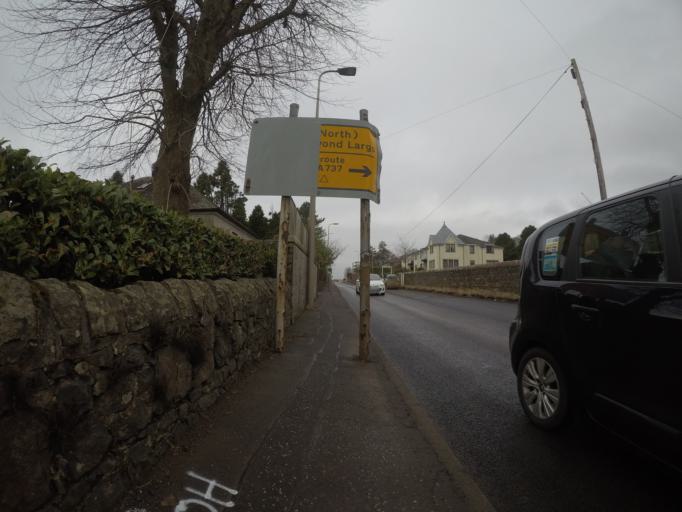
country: GB
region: Scotland
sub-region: North Ayrshire
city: Largs
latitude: 55.7834
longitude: -4.8571
